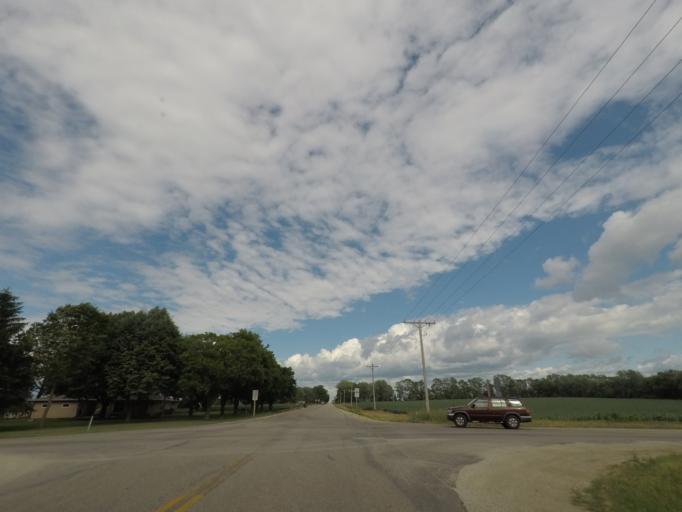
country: US
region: Wisconsin
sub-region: Rock County
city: Janesville
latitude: 42.7013
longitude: -89.1310
